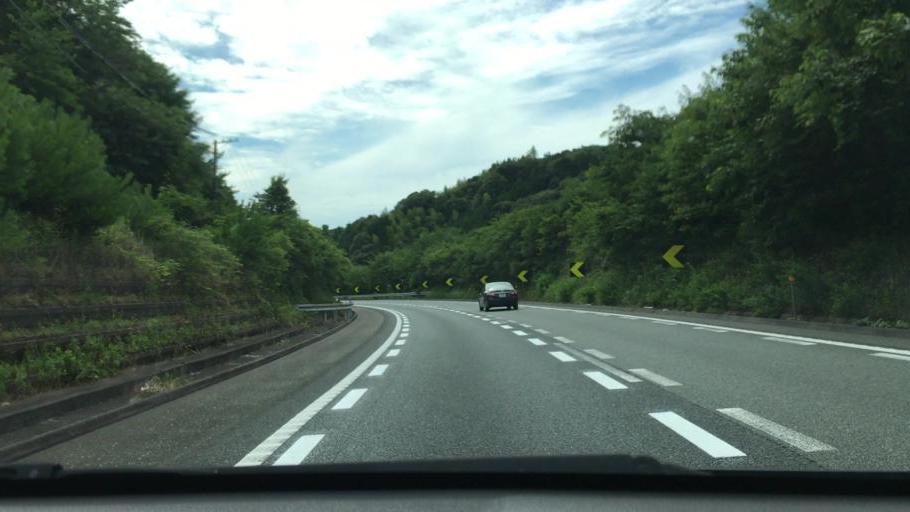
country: JP
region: Yamaguchi
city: Yamaguchi-shi
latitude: 34.1321
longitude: 131.4501
